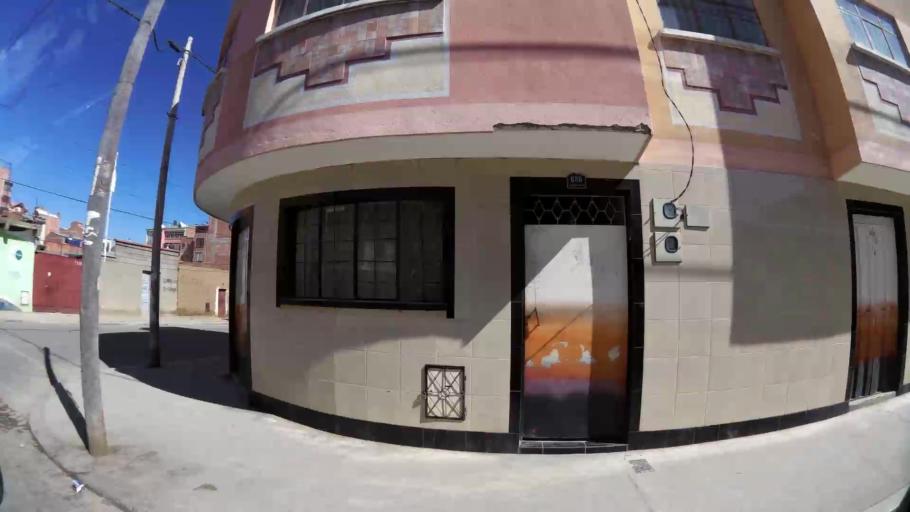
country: BO
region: La Paz
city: La Paz
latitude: -16.5186
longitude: -68.1552
